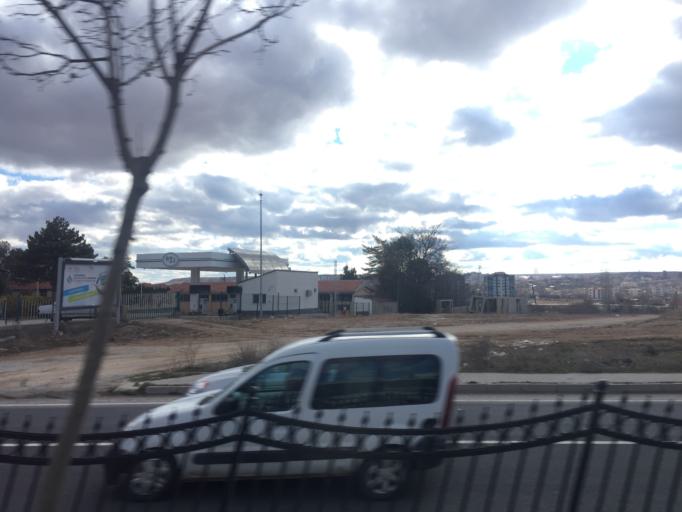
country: TR
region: Kirsehir
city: Kirsehir
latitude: 39.1633
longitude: 34.1564
